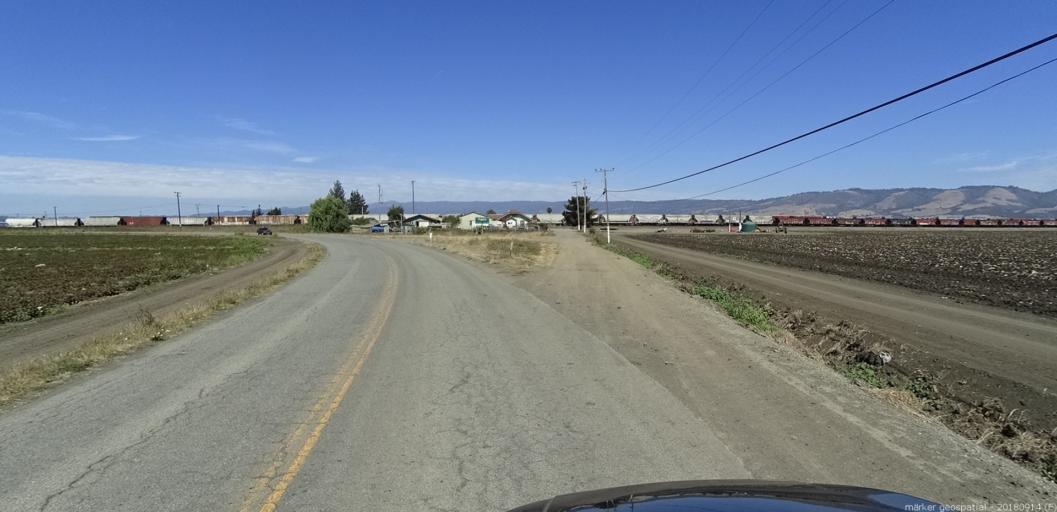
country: US
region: California
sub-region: Monterey County
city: Pajaro
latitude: 36.8951
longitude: -121.7357
